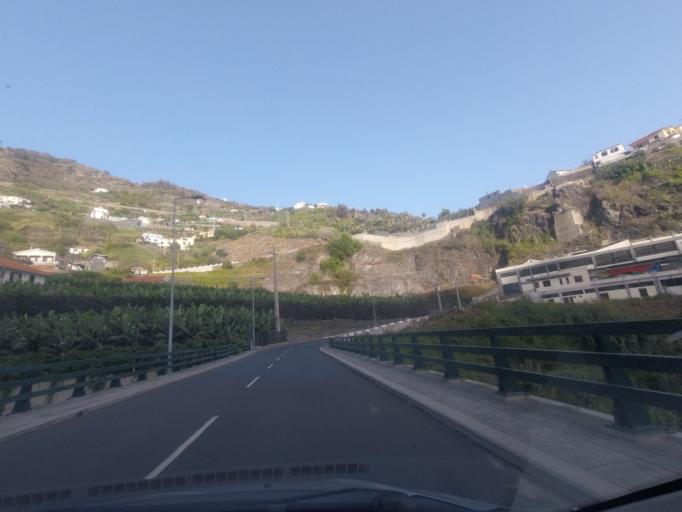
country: PT
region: Madeira
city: Ponta do Sol
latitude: 32.6835
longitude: -17.0747
